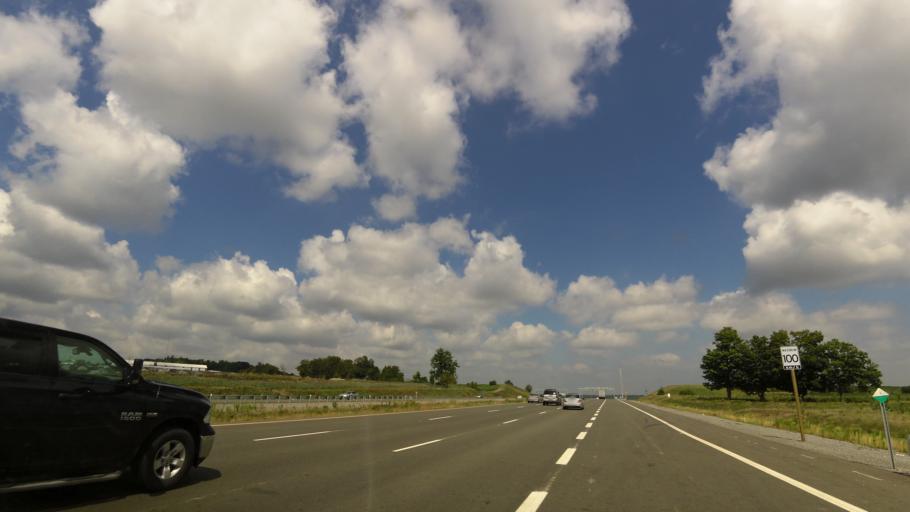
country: CA
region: Ontario
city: Pickering
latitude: 43.9230
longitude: -79.0928
